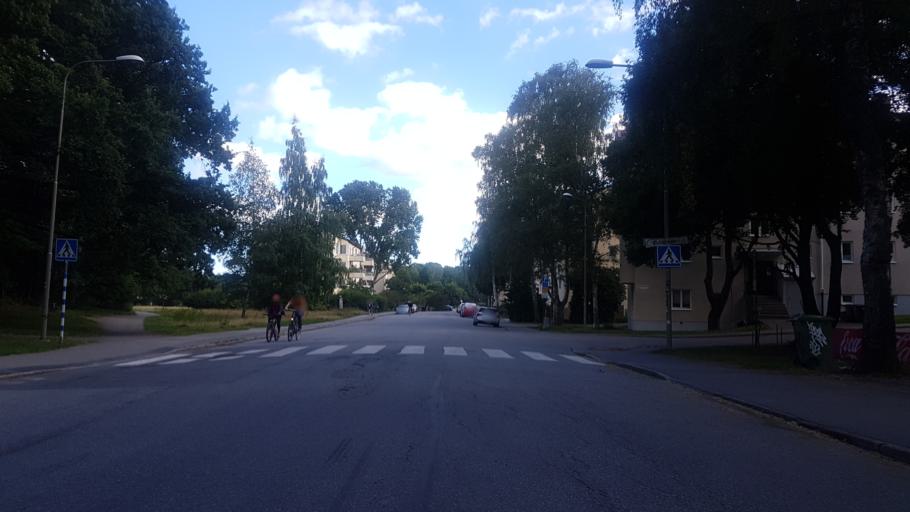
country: SE
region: Stockholm
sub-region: Stockholms Kommun
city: OEstermalm
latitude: 59.2932
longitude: 18.1069
